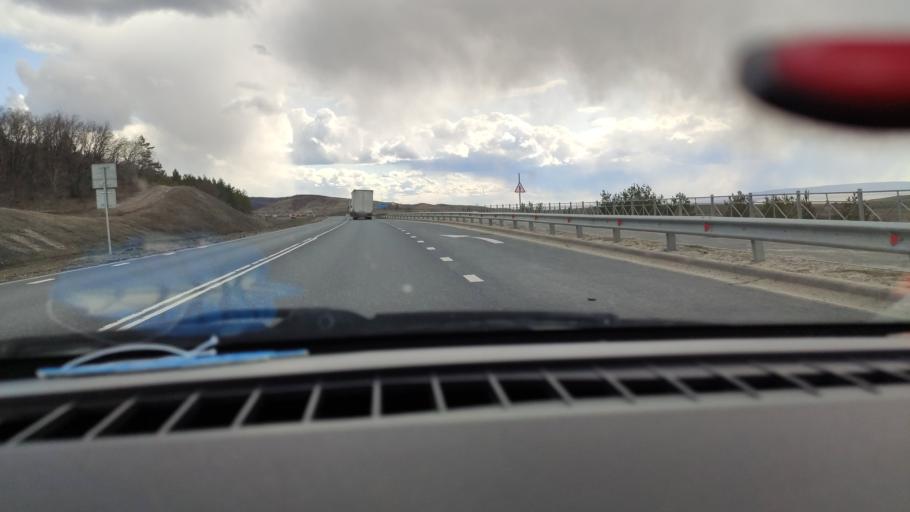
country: RU
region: Saratov
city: Alekseyevka
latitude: 52.3851
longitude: 47.9733
